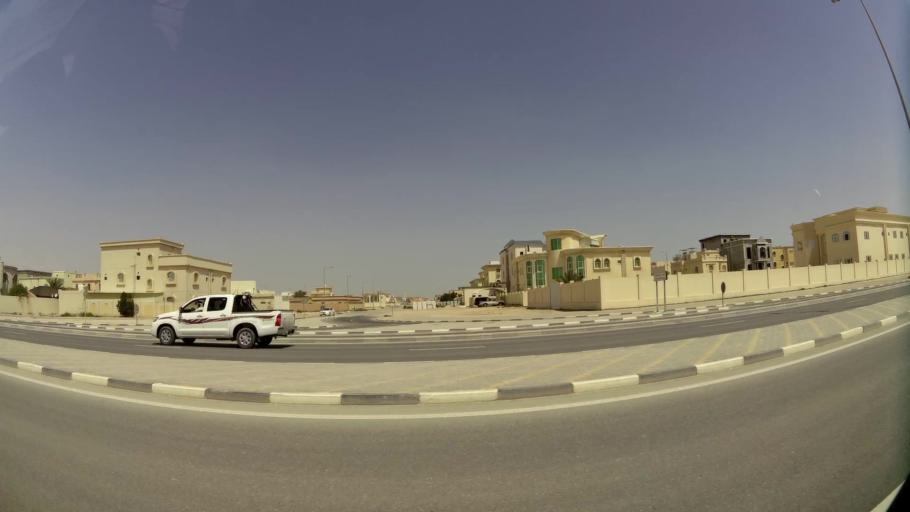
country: QA
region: Baladiyat Umm Salal
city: Umm Salal Muhammad
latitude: 25.3827
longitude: 51.4562
